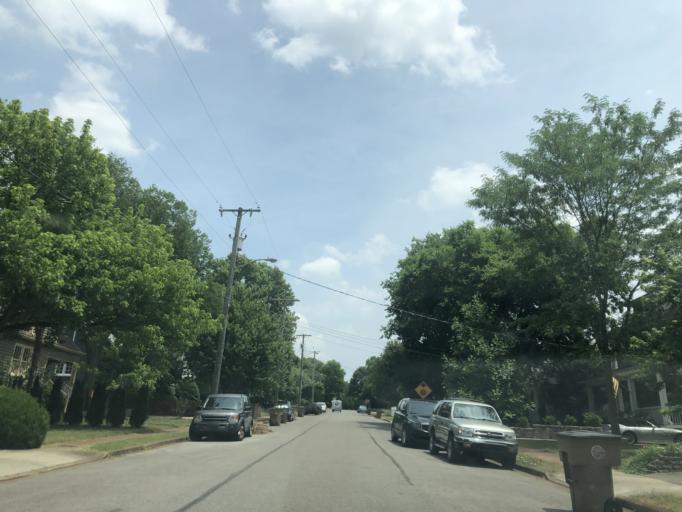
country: US
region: Tennessee
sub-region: Davidson County
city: Nashville
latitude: 36.1291
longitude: -86.8090
